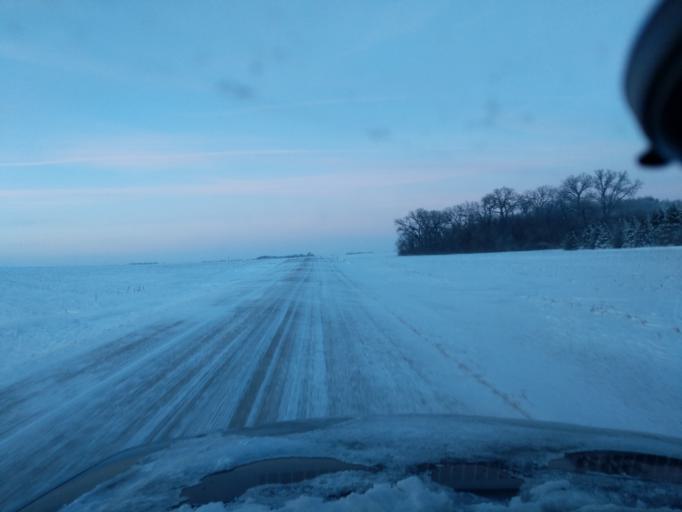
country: US
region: Minnesota
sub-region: Renville County
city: Renville
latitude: 44.7278
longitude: -95.3587
